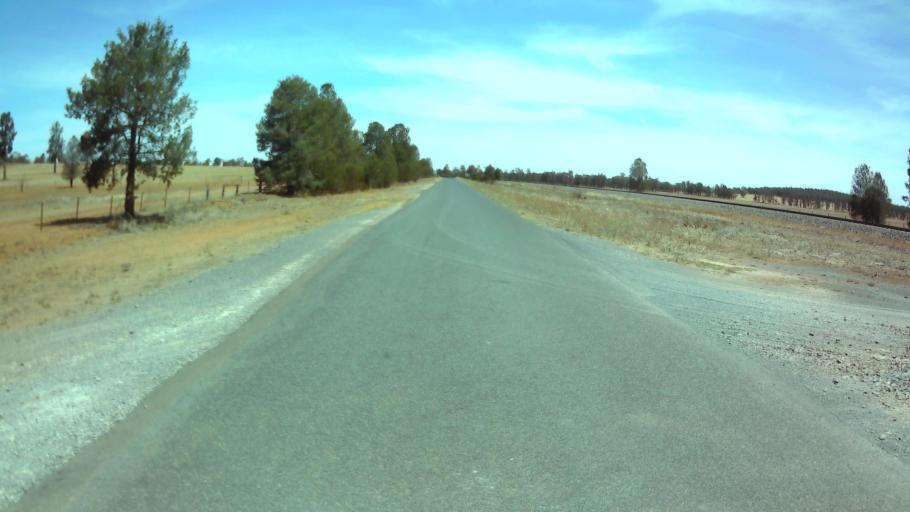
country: AU
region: New South Wales
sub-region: Weddin
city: Grenfell
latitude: -33.7736
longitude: 147.7558
